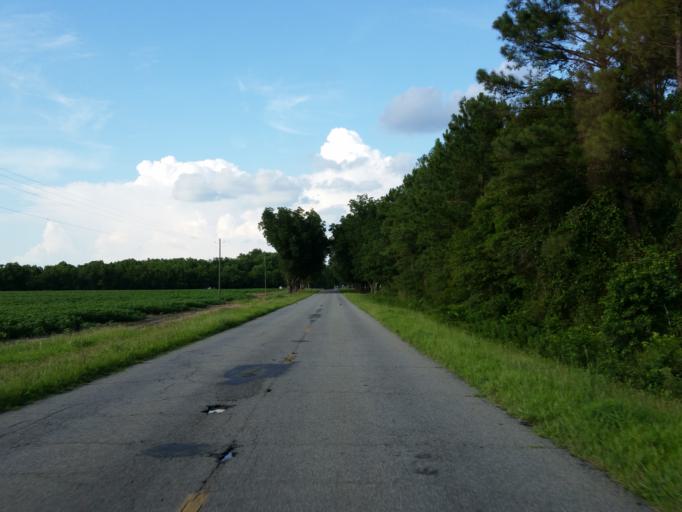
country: US
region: Georgia
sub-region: Dooly County
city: Vienna
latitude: 32.0766
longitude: -83.8089
